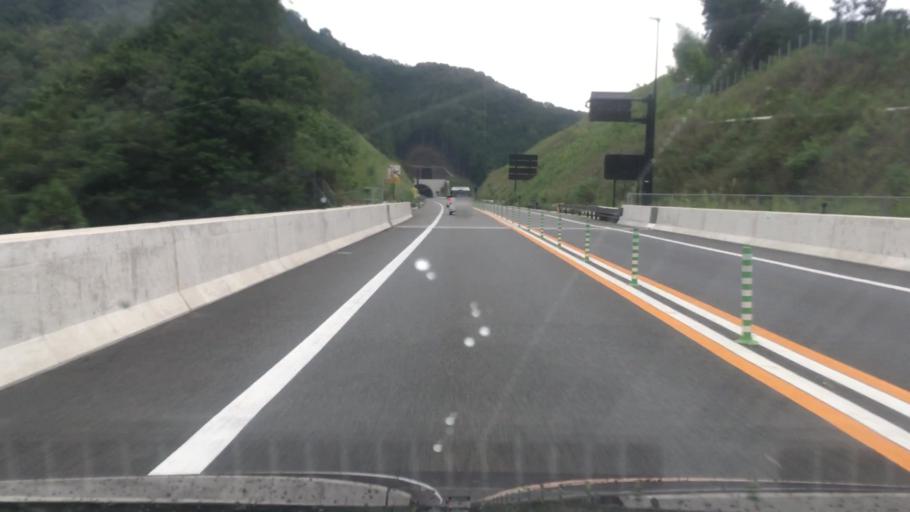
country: JP
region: Hyogo
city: Toyooka
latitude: 35.4392
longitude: 134.7678
